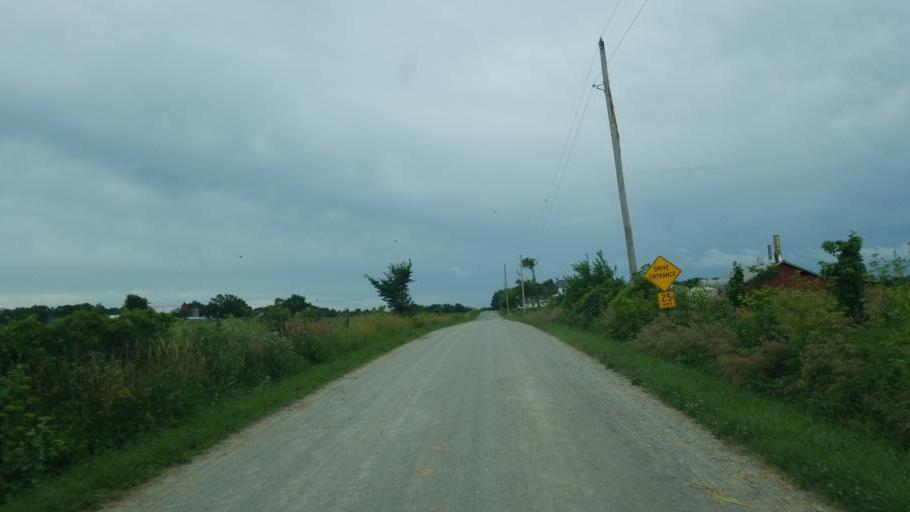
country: US
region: Ohio
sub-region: Huron County
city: Greenwich
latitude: 40.9361
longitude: -82.4312
